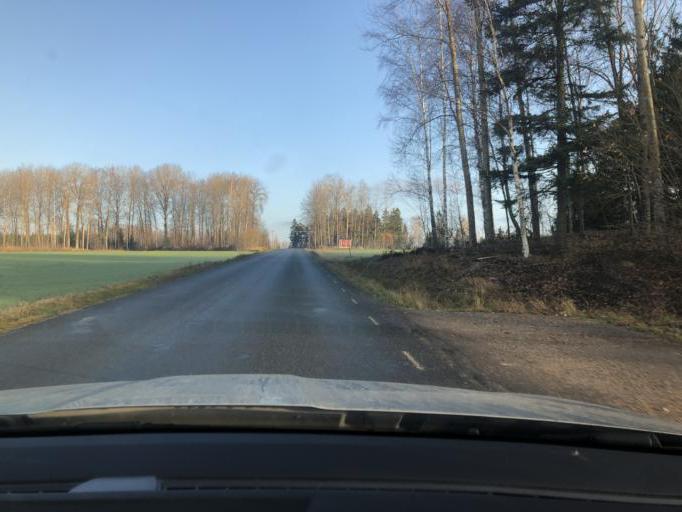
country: SE
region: Soedermanland
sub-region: Flens Kommun
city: Halleforsnas
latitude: 59.0305
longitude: 16.3942
